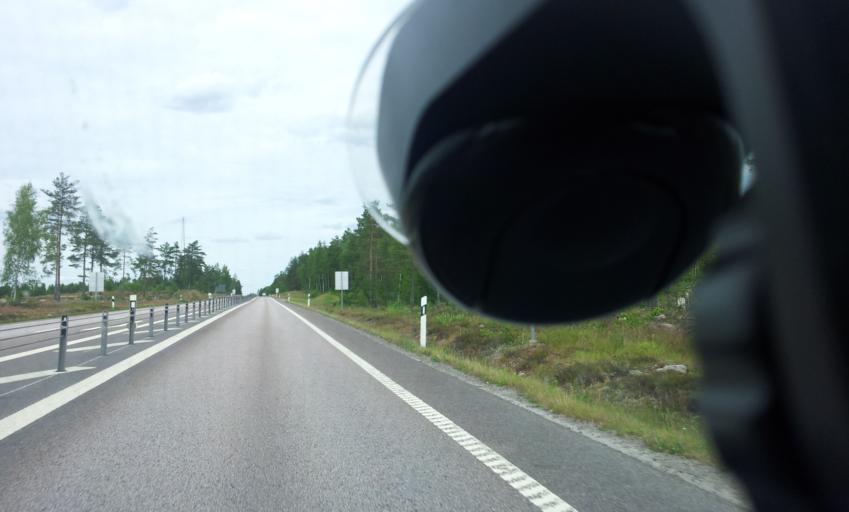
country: SE
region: Kalmar
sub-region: Oskarshamns Kommun
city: Oskarshamn
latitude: 57.3996
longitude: 16.4796
